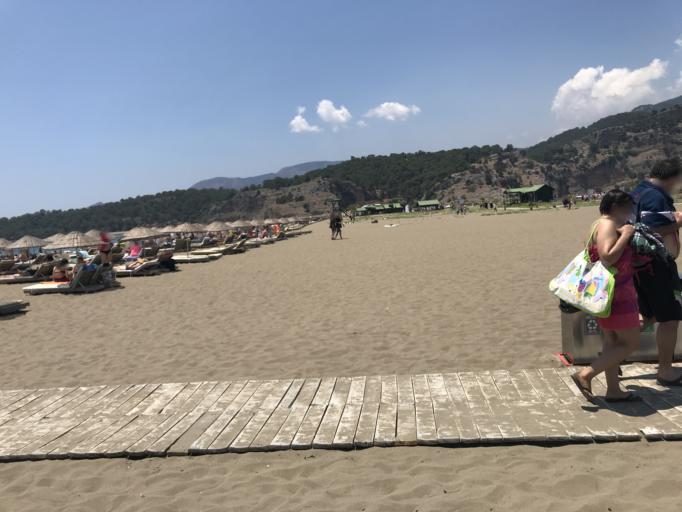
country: TR
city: Dalyan
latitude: 36.8000
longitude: 28.6082
